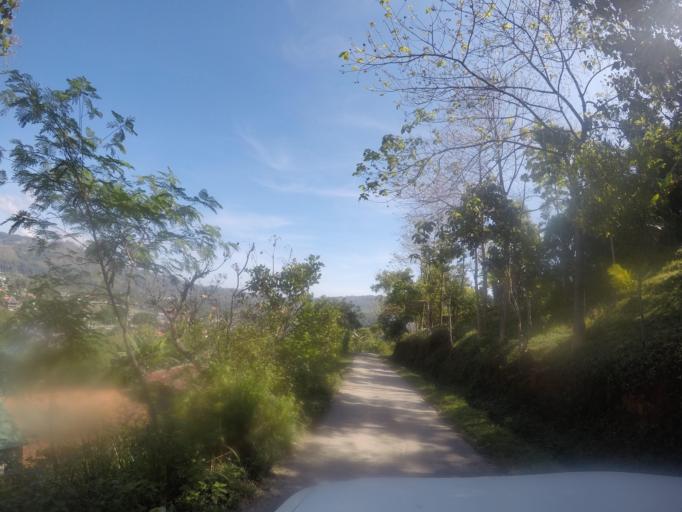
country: TL
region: Ermera
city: Gleno
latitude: -8.7273
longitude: 125.4374
